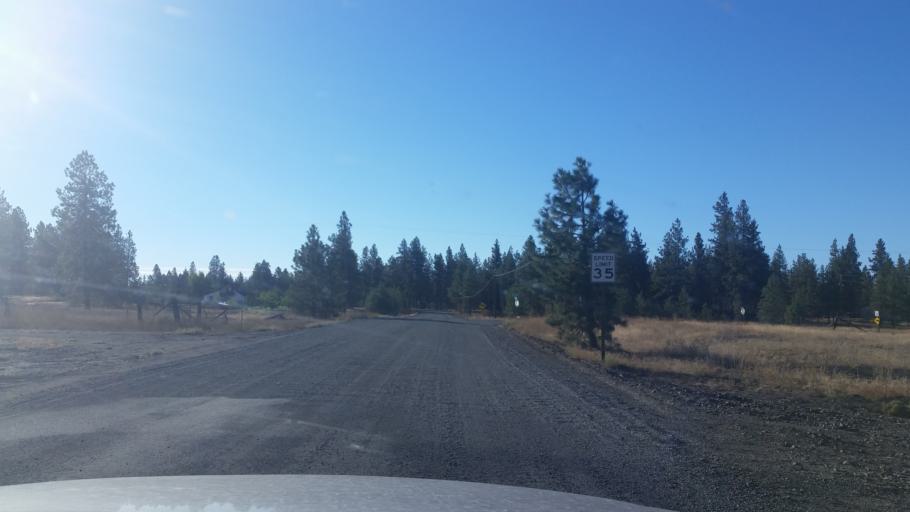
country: US
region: Washington
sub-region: Spokane County
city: Medical Lake
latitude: 47.4342
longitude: -117.7820
